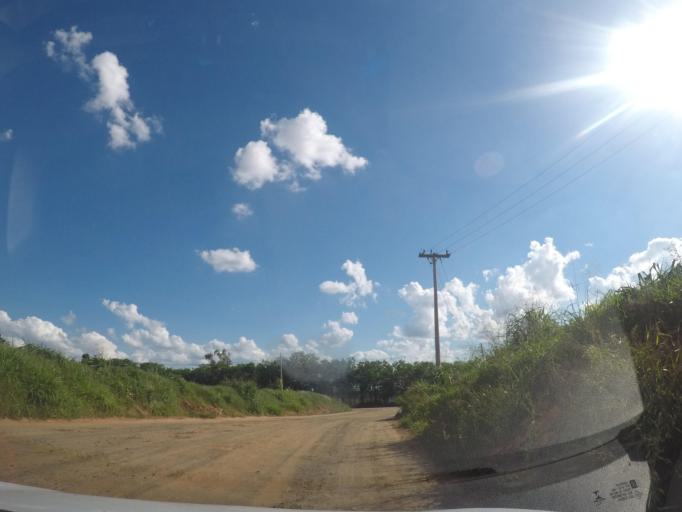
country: BR
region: Sao Paulo
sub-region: Sumare
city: Sumare
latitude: -22.8511
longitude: -47.3279
